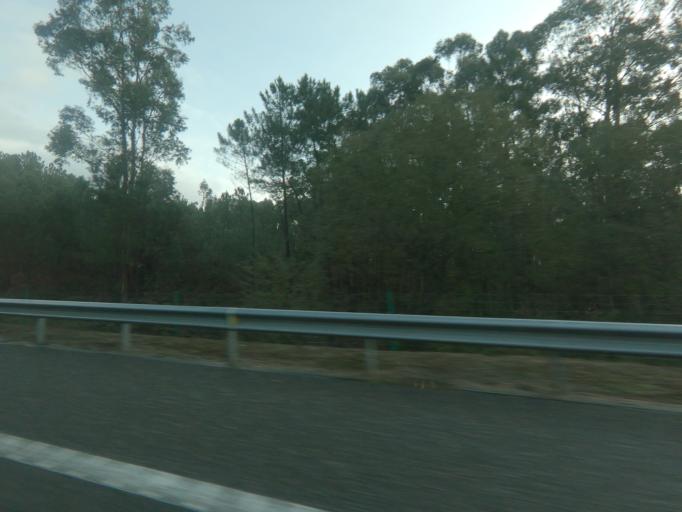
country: ES
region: Galicia
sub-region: Provincia de Pontevedra
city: Tui
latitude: 42.1001
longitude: -8.6438
